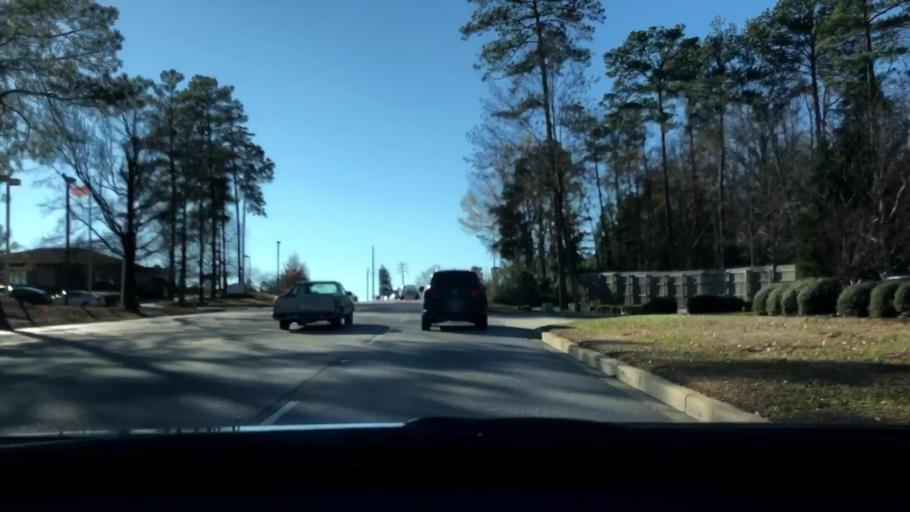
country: US
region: South Carolina
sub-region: Lexington County
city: Irmo
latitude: 34.0677
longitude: -81.1667
